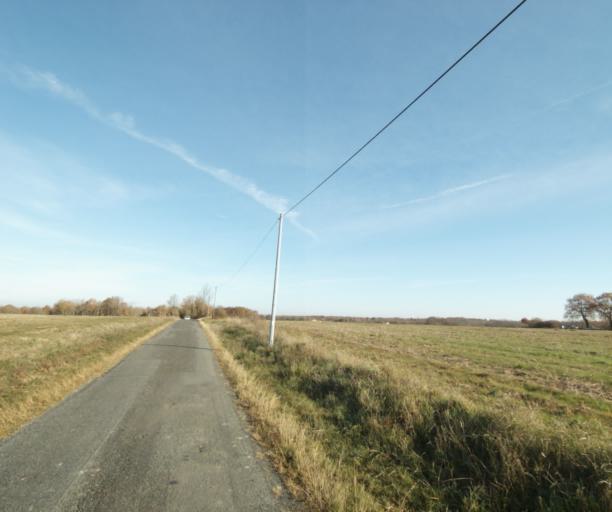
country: FR
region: Poitou-Charentes
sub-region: Departement de la Charente-Maritime
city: Cherac
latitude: 45.7480
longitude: -0.4850
